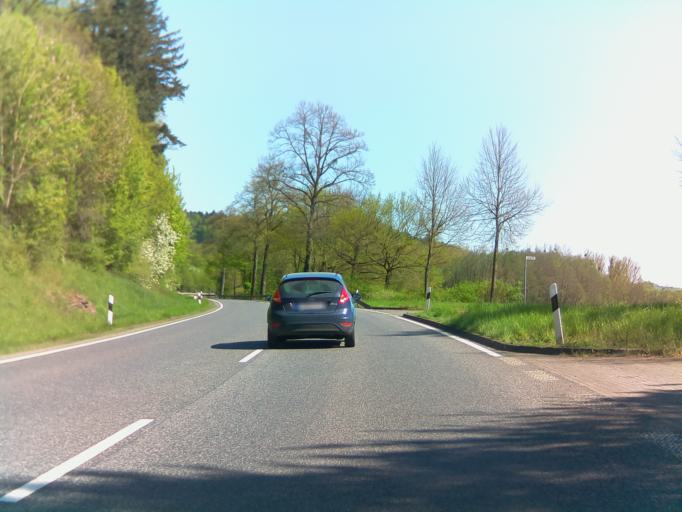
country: DE
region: Hesse
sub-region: Regierungsbezirk Giessen
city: Alsfeld
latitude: 50.7183
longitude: 9.2919
